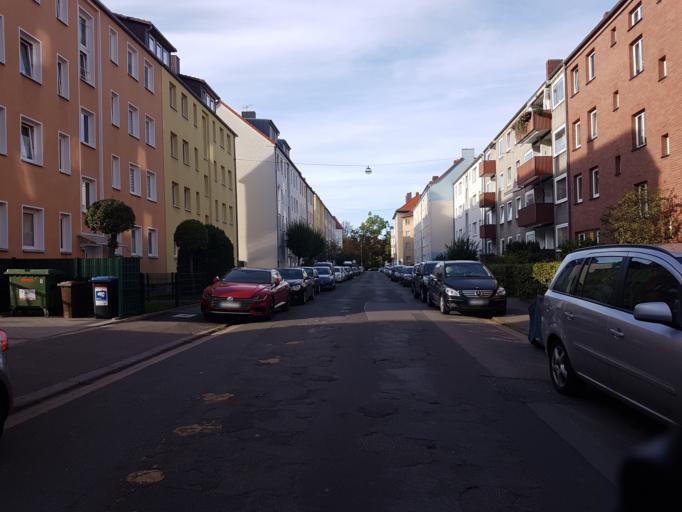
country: DE
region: Lower Saxony
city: Hannover
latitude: 52.3826
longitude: 9.7432
